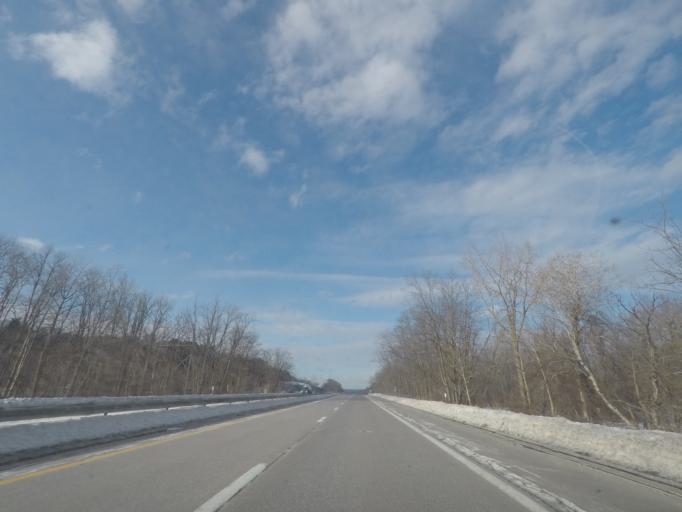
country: US
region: New York
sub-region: Schenectady County
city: Scotia
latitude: 42.8194
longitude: -73.9885
